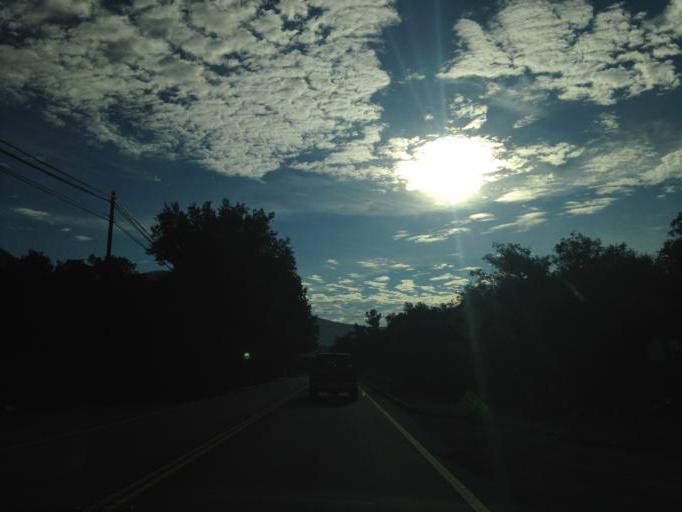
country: US
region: California
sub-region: San Diego County
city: Valley Center
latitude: 33.3409
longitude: -117.0144
